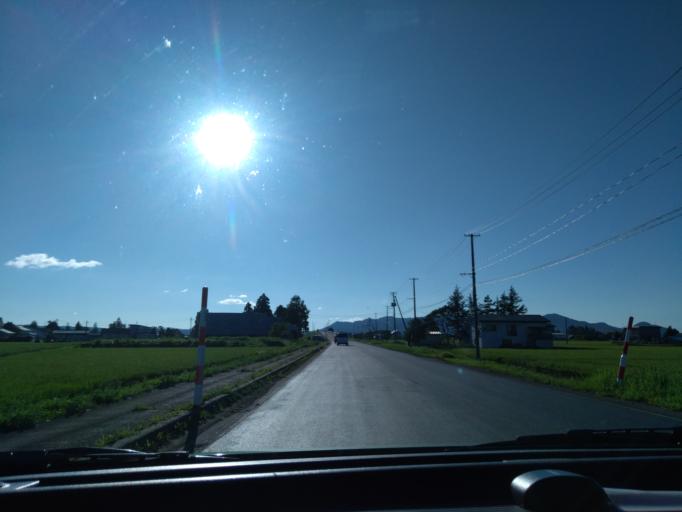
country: JP
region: Akita
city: Omagari
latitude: 39.4224
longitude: 140.5111
